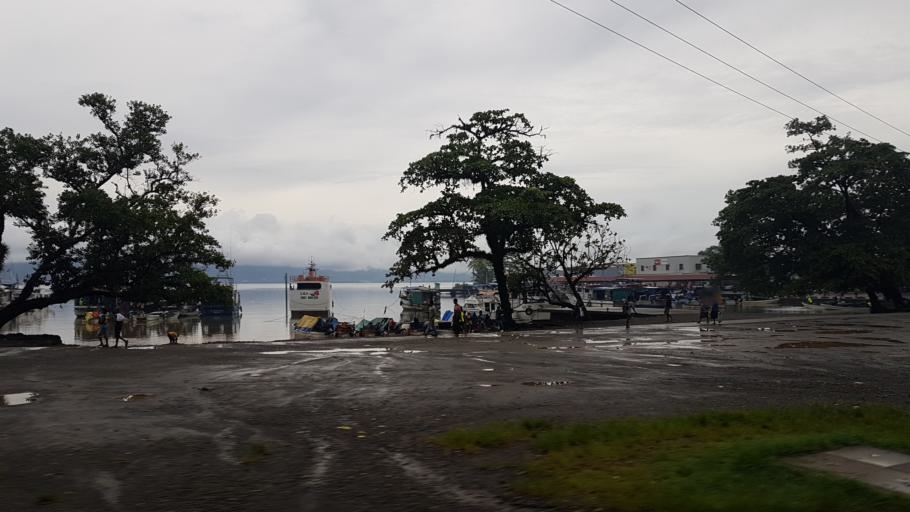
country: PG
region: Milne Bay
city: Alotau
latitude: -10.3083
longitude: 150.4544
